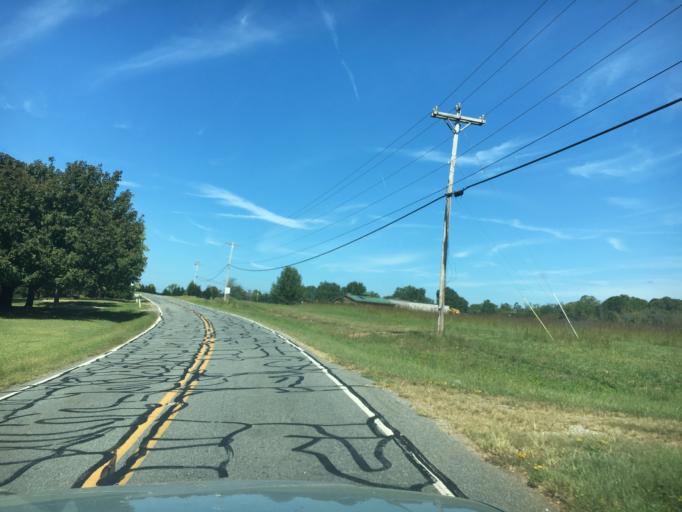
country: US
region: North Carolina
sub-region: Rutherford County
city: Spindale
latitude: 35.3187
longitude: -81.9353
